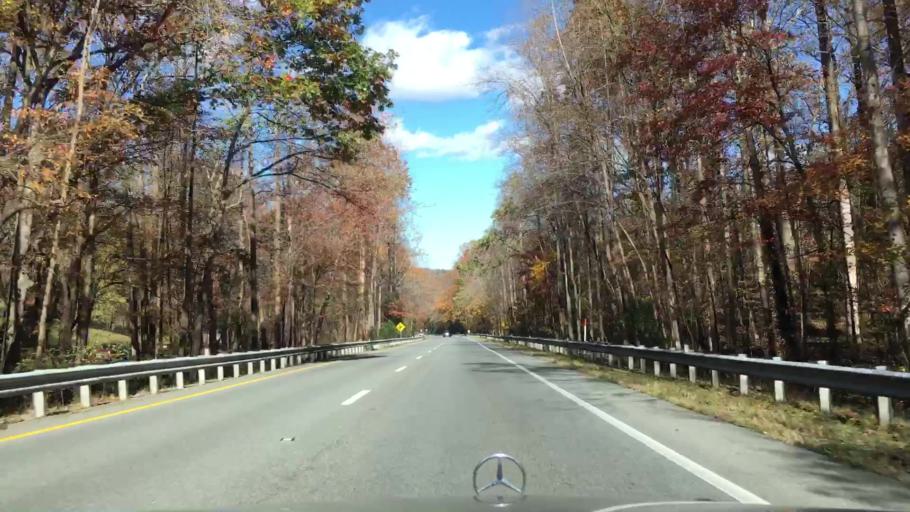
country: US
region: Virginia
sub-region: Albemarle County
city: Crozet
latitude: 37.9454
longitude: -78.6648
